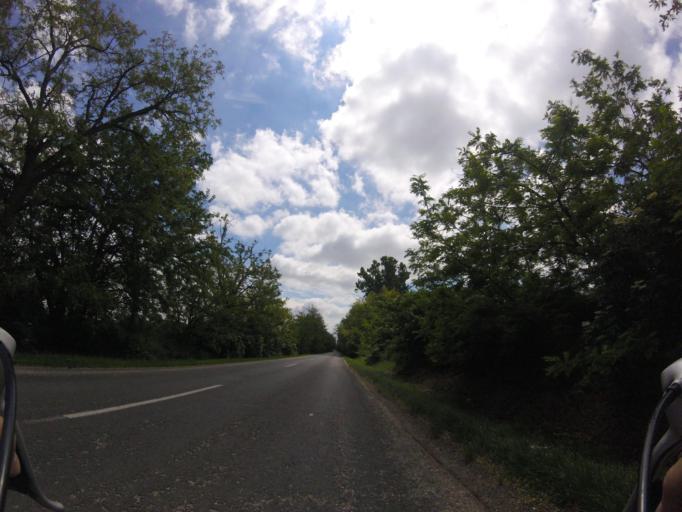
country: HU
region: Fejer
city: Sarosd
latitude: 47.0777
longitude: 18.6092
